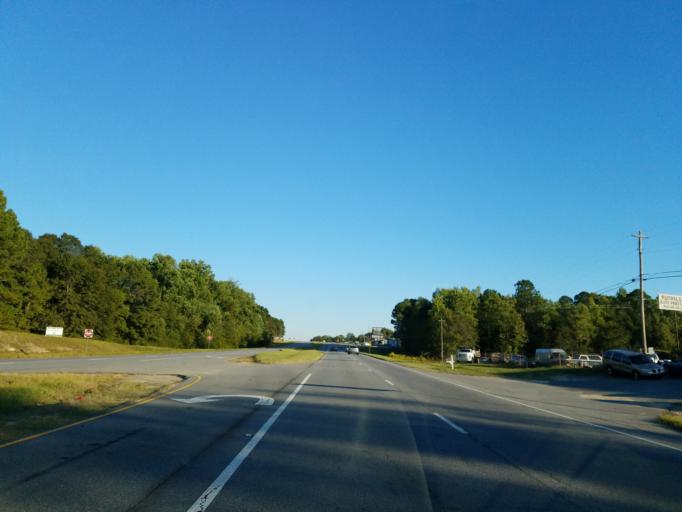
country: US
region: Georgia
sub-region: Worth County
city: Sylvester
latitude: 31.5218
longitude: -83.7895
